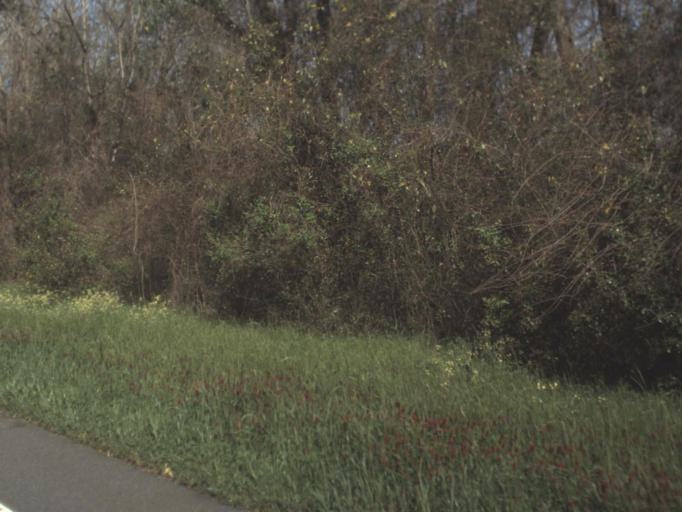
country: US
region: Alabama
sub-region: Houston County
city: Cottonwood
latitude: 30.9447
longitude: -85.2756
